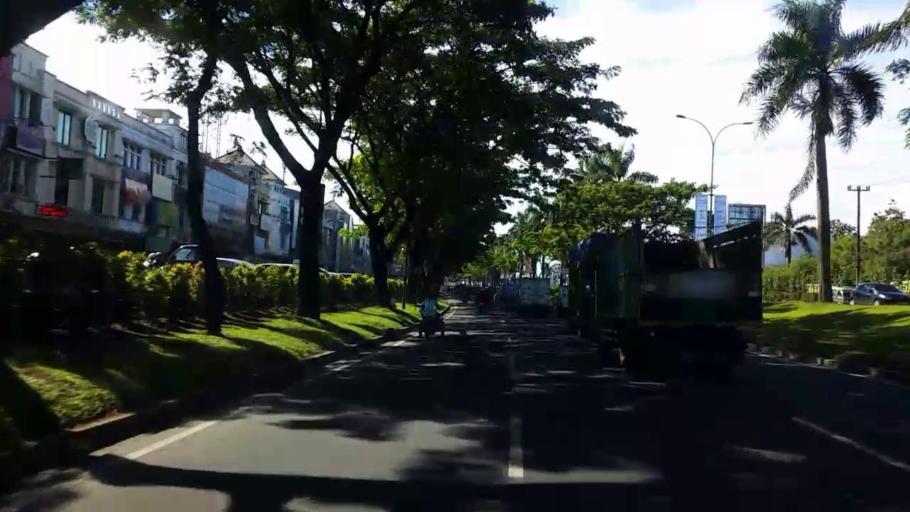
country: ID
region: West Java
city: Serpong
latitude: -6.3010
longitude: 106.6683
